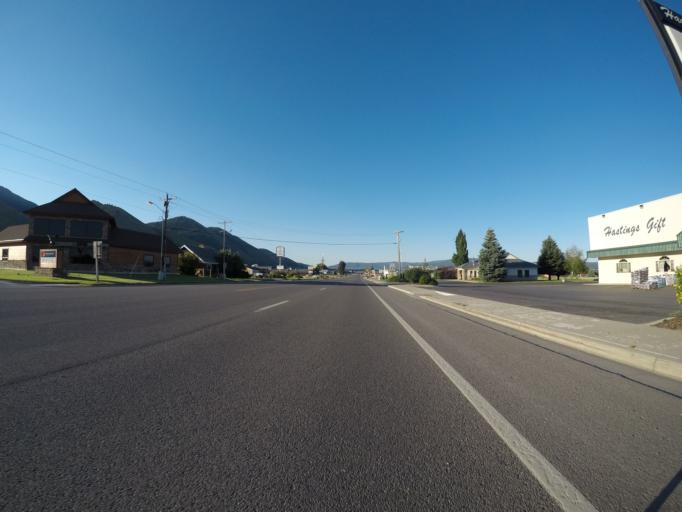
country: US
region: Wyoming
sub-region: Lincoln County
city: Afton
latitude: 42.7175
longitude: -110.9336
